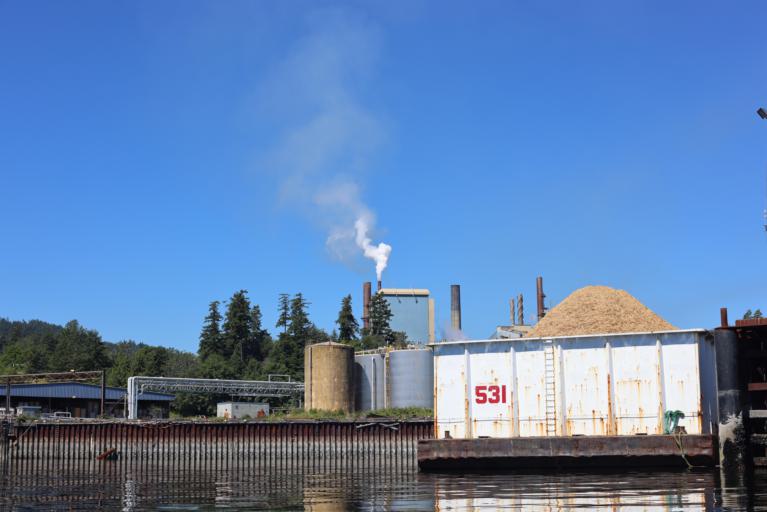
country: CA
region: British Columbia
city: North Cowichan
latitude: 48.8752
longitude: -123.6412
